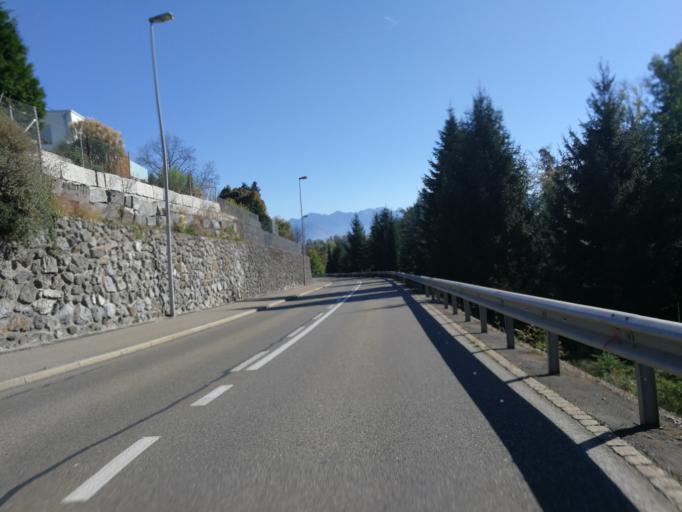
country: CH
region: Zurich
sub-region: Bezirk Meilen
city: Hombrechtikon
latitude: 47.2482
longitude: 8.7695
